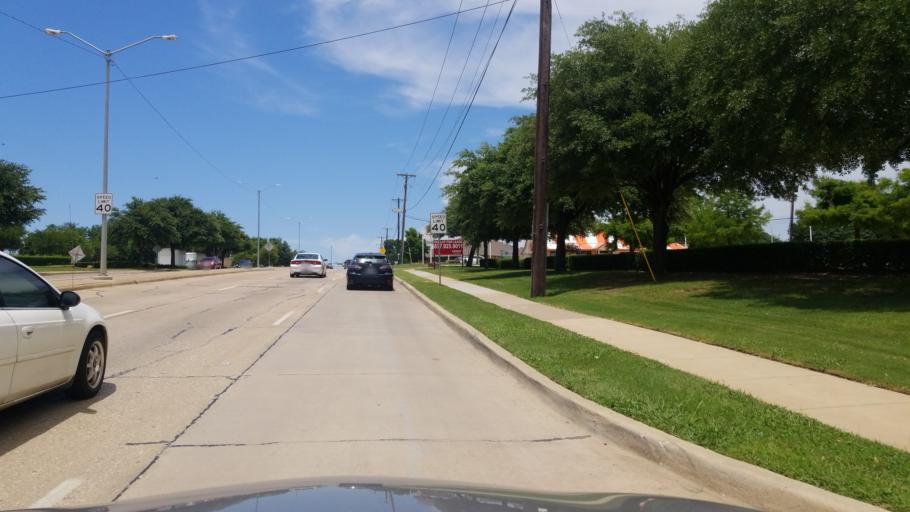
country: US
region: Texas
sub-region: Dallas County
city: Grand Prairie
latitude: 32.6779
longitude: -97.0068
